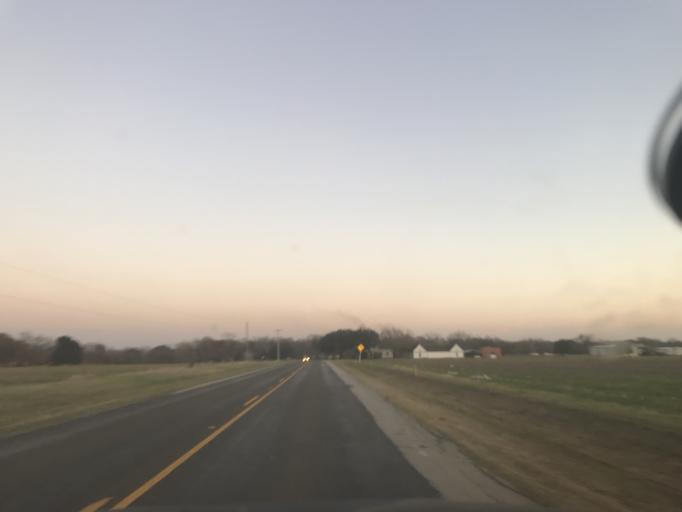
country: US
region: Texas
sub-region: Williamson County
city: Hutto
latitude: 30.4970
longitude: -97.5025
